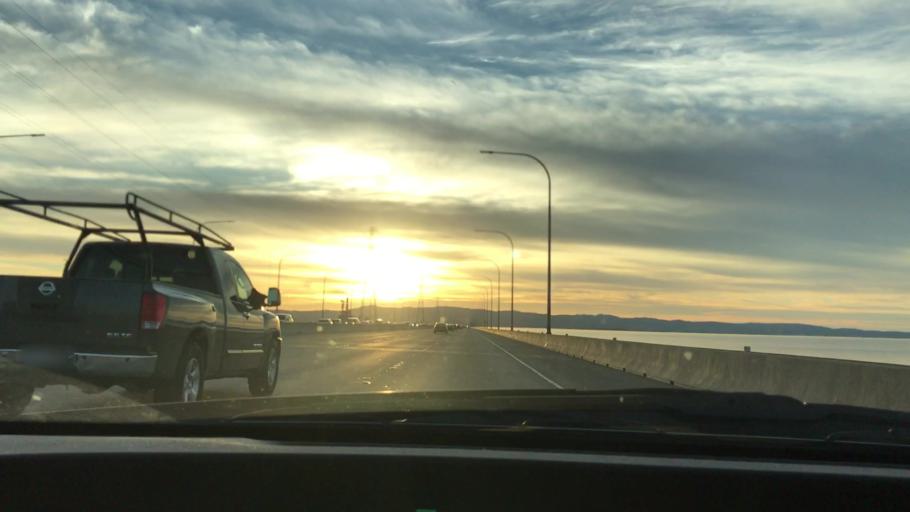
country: US
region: California
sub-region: Alameda County
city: San Lorenzo
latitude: 37.6147
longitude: -122.1632
